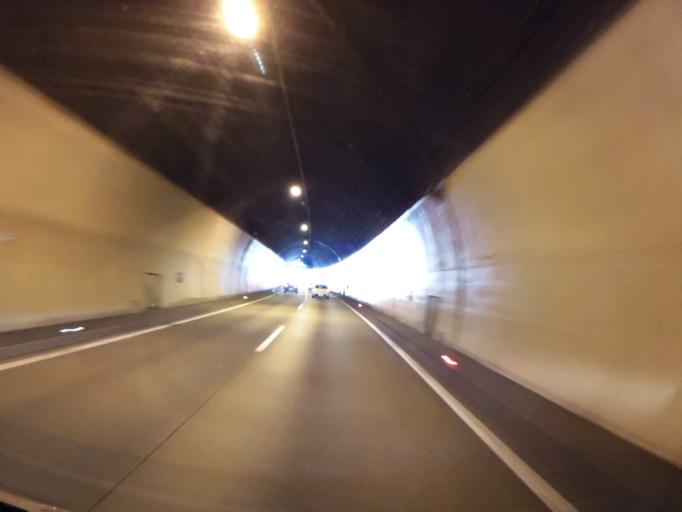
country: AT
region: Styria
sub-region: Politischer Bezirk Graz-Umgebung
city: Deutschfeistritz
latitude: 47.1974
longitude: 15.3221
